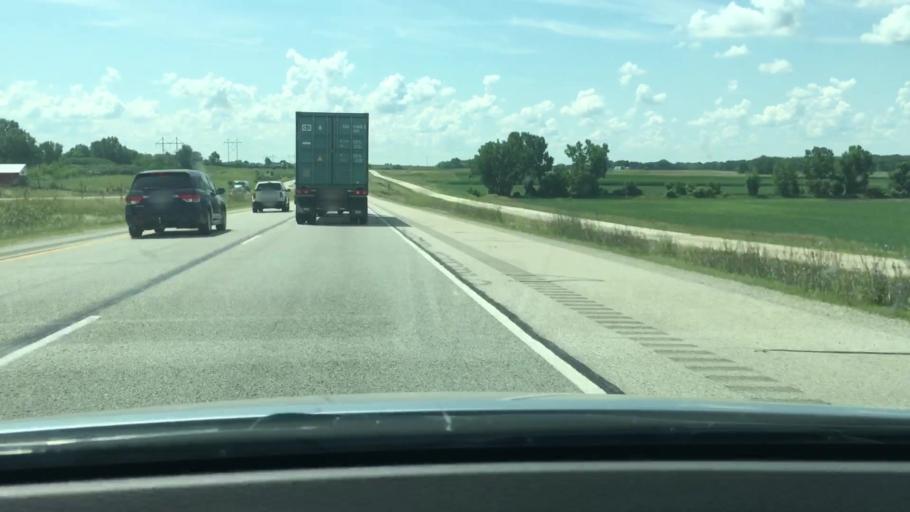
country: US
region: Wisconsin
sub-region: Fond du Lac County
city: Rosendale
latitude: 43.8884
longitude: -88.5841
